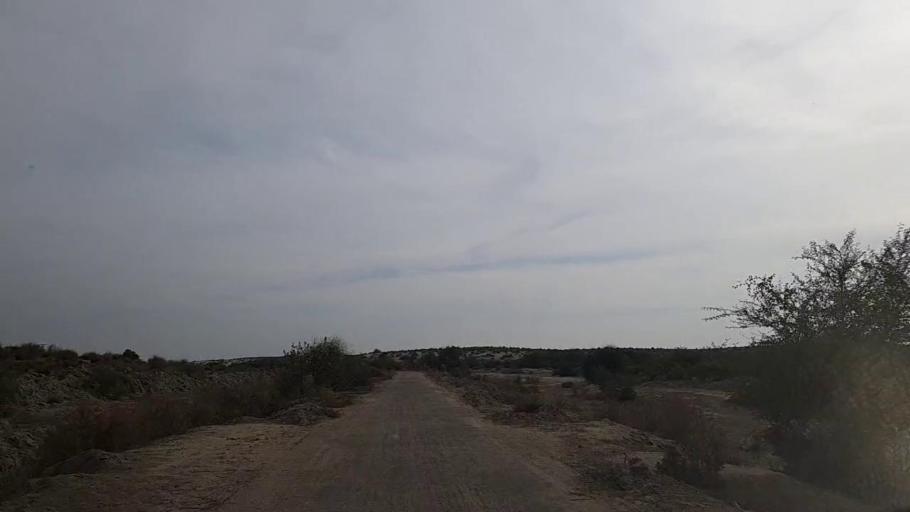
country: PK
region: Sindh
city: Jam Sahib
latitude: 26.4420
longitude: 68.6231
